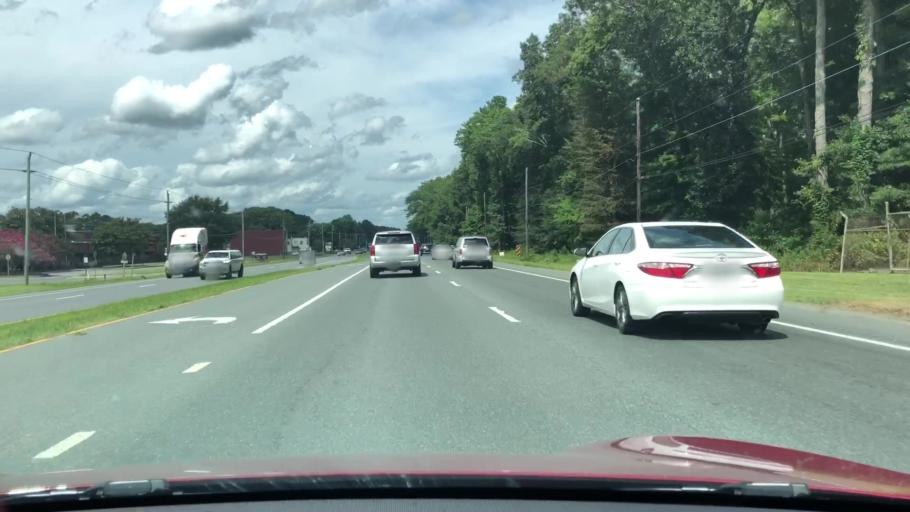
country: US
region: Virginia
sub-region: Accomack County
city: Wattsville
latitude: 37.9236
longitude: -75.5491
